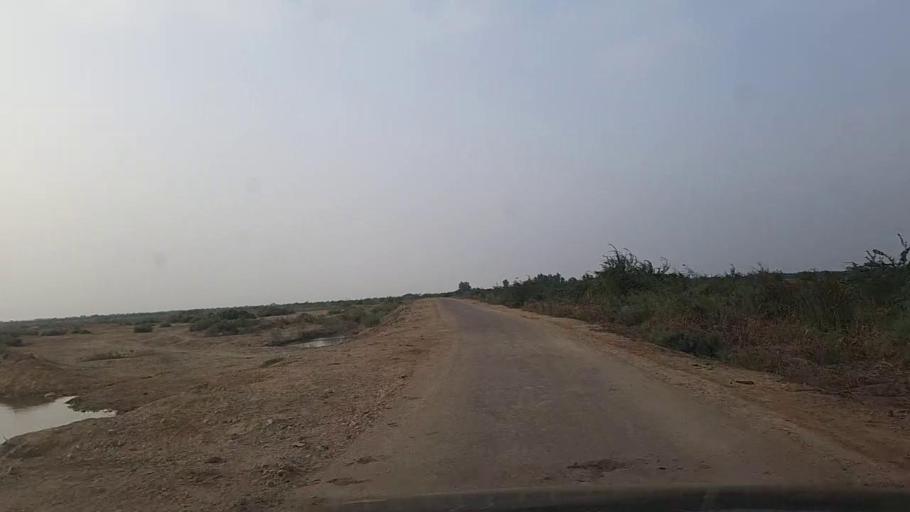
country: PK
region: Sindh
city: Gharo
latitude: 24.7759
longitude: 67.7376
